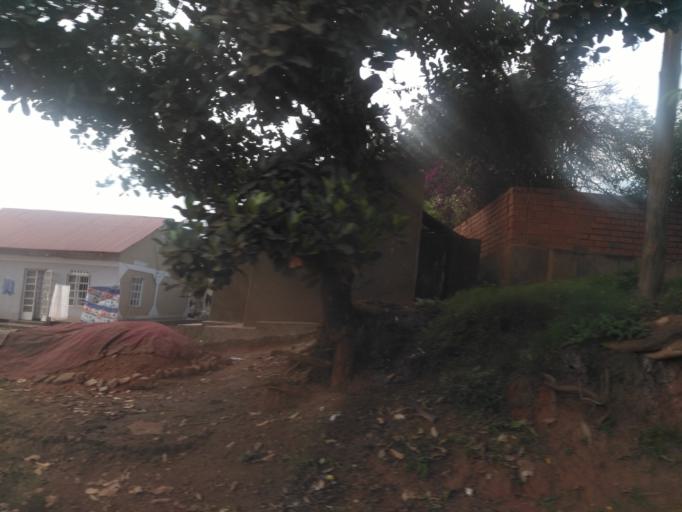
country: UG
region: Central Region
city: Kampala Central Division
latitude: 0.3460
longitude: 32.5949
